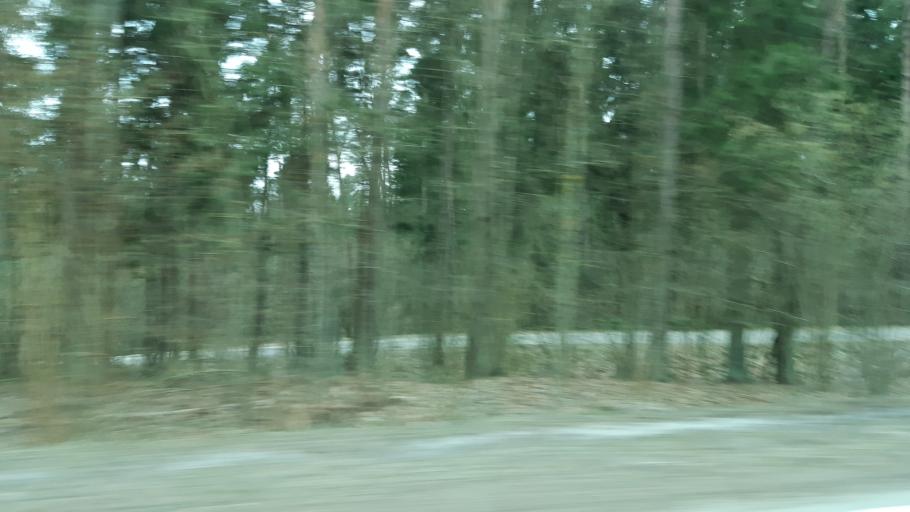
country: PL
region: Podlasie
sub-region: Suwalki
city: Suwalki
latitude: 54.3089
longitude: 22.9573
